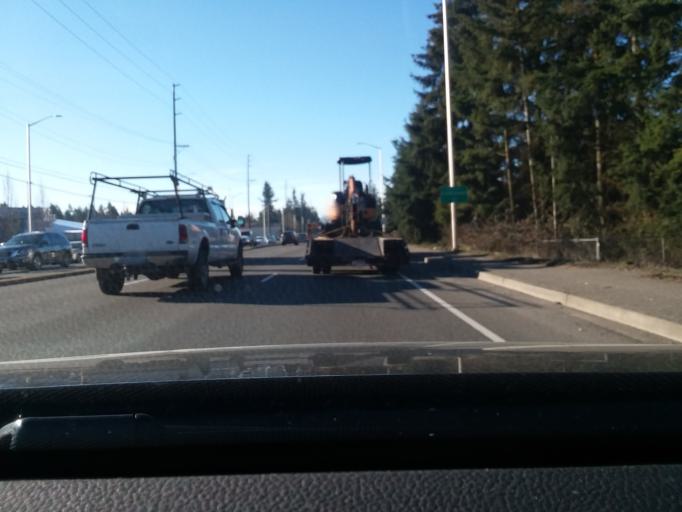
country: US
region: Washington
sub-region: Pierce County
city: Frederickson
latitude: 47.1108
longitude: -122.3577
